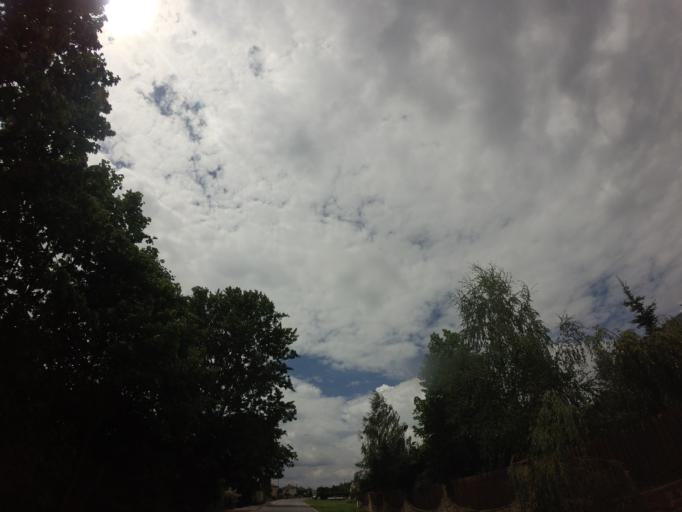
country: PL
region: Lublin Voivodeship
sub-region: Powiat pulawski
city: Kazimierz Dolny
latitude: 51.2841
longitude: 21.9418
